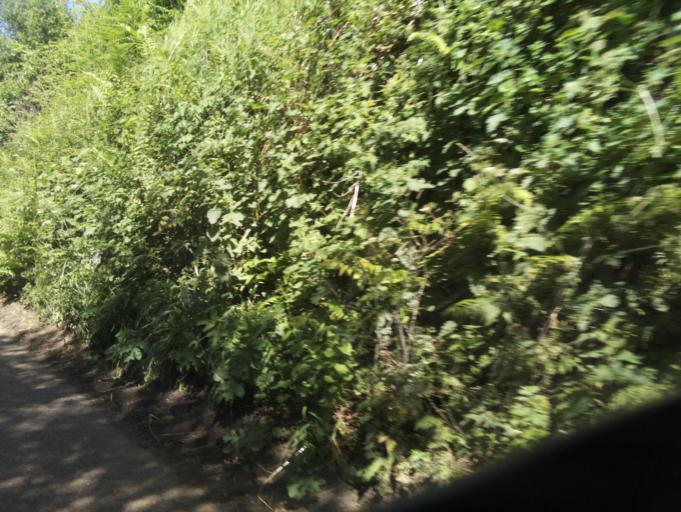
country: GB
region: England
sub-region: Devon
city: Newton Poppleford
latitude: 50.7057
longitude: -3.2674
